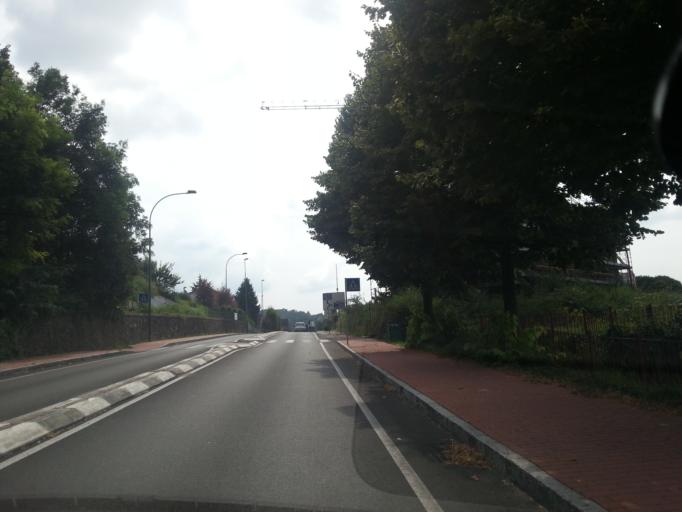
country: IT
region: Lombardy
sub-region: Provincia di Lecco
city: Oggiono
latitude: 45.7851
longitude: 9.3430
